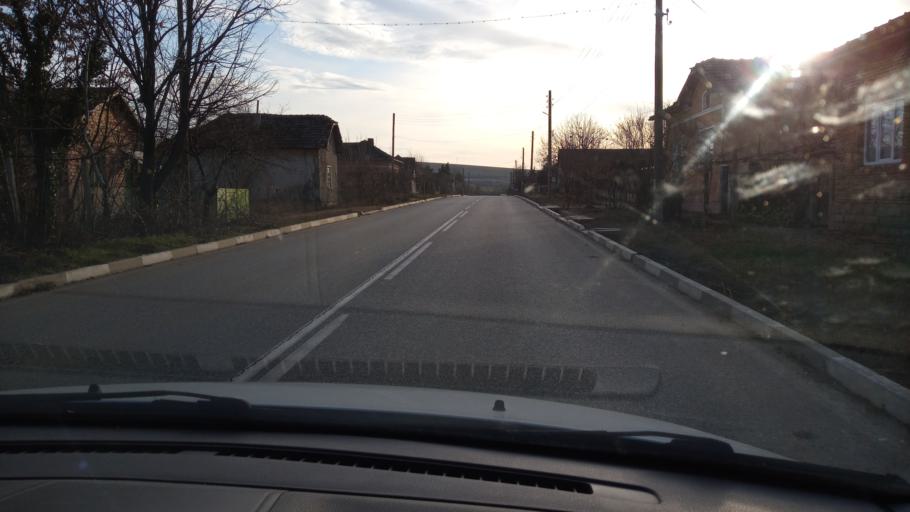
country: BG
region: Pleven
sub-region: Obshtina Pleven
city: Slavyanovo
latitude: 43.5506
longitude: 24.8635
